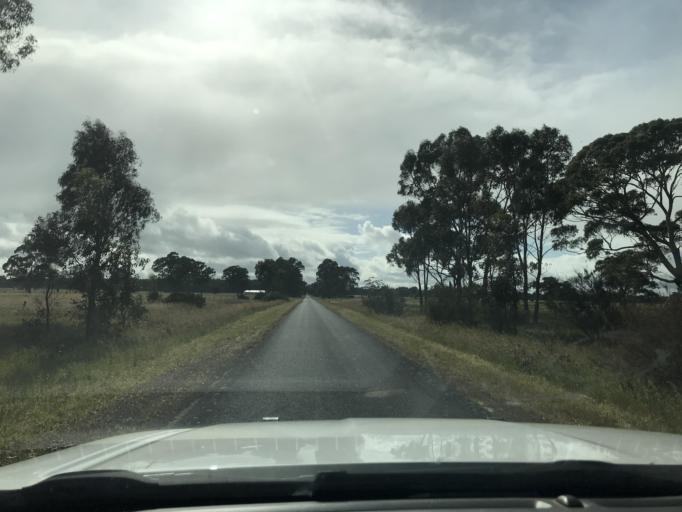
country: AU
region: South Australia
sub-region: Wattle Range
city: Penola
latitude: -37.1853
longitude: 141.2077
